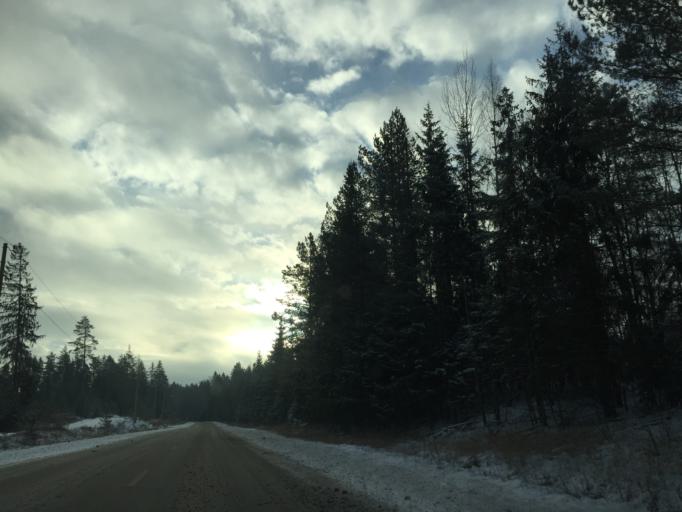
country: LV
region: Amatas Novads
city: Drabesi
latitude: 57.2243
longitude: 25.2835
